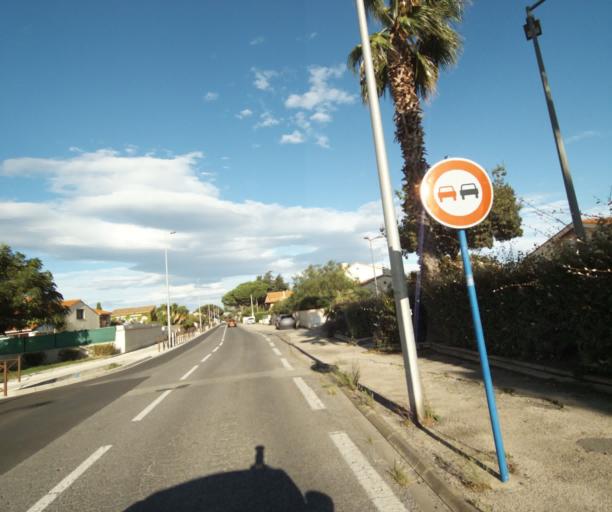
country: FR
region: Languedoc-Roussillon
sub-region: Departement des Pyrenees-Orientales
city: Argelers
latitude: 42.5462
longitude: 3.0311
